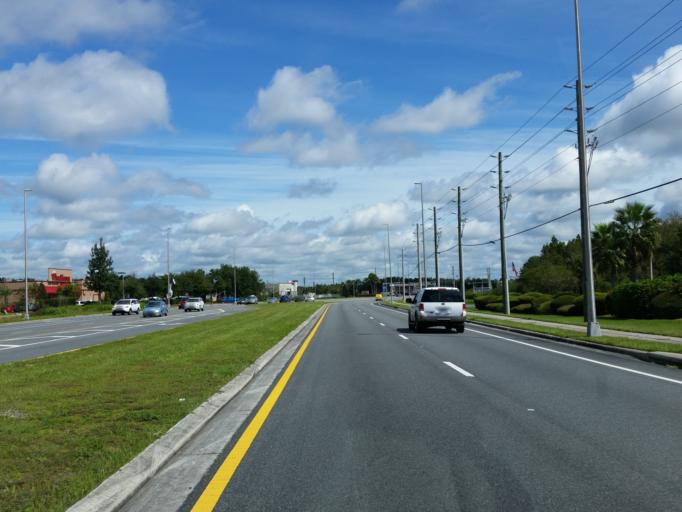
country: US
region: Florida
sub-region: Pasco County
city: Wesley Chapel
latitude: 28.2354
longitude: -82.3691
